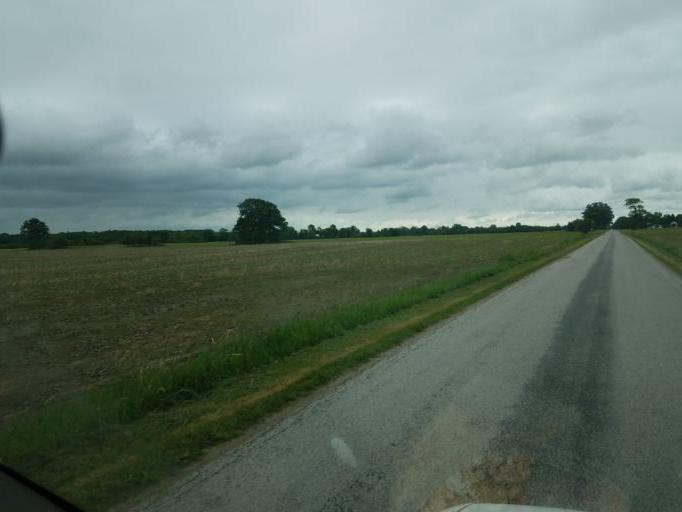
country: US
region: Ohio
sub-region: Morrow County
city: Cardington
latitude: 40.5556
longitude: -82.9194
